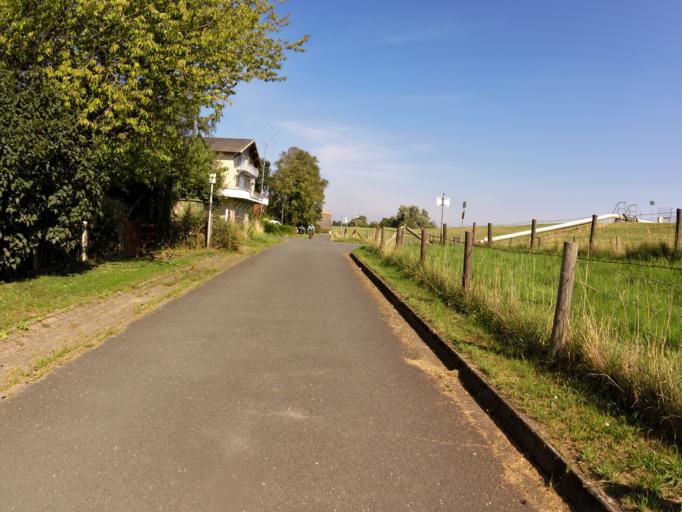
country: DE
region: Lower Saxony
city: Elsfleth
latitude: 53.2674
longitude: 8.4799
